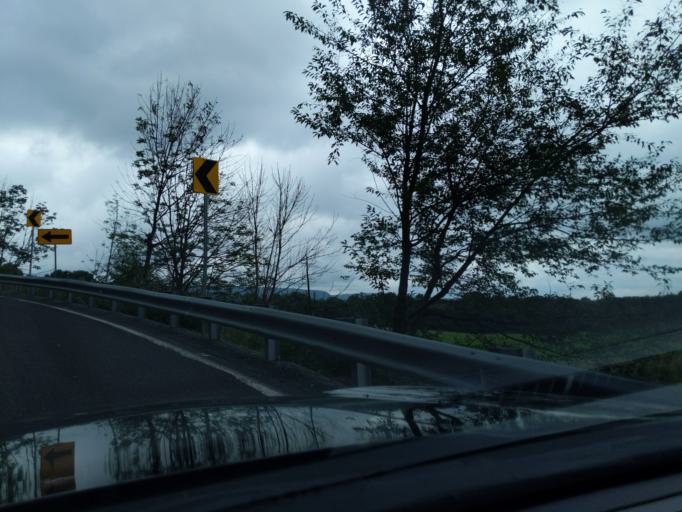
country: US
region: Pennsylvania
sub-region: Blair County
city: Claysburg
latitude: 40.3563
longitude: -78.5089
